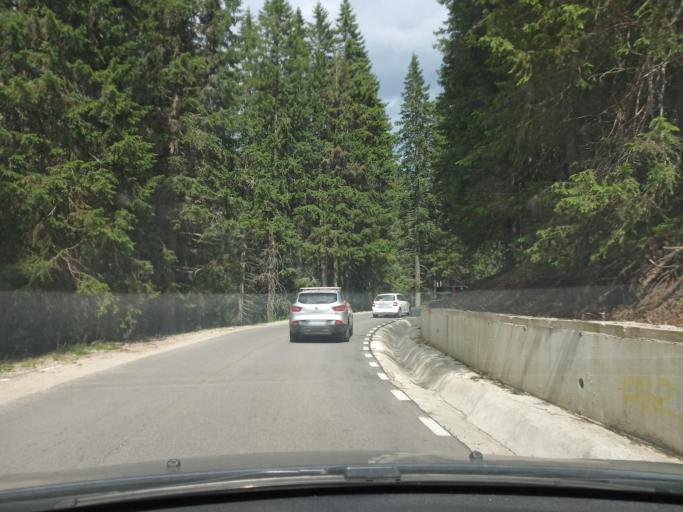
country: RO
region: Dambovita
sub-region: Comuna Moroeni
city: Glod
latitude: 45.3257
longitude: 25.4556
